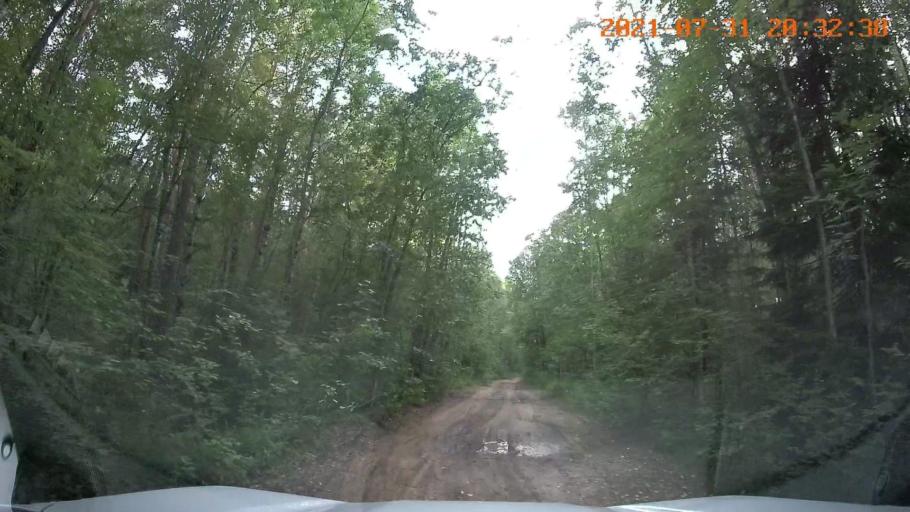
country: RU
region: Republic of Karelia
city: Shal'skiy
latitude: 61.6615
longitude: 36.2726
